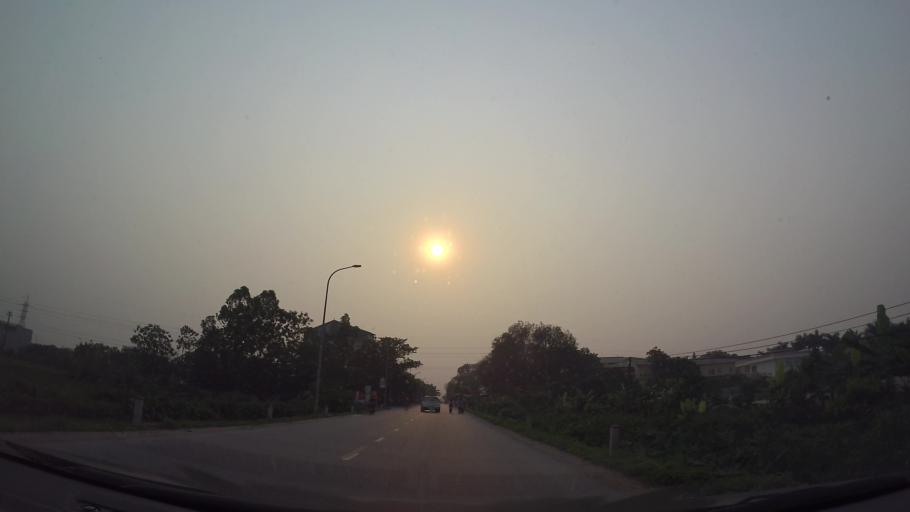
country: VN
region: Ha Noi
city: Thuong Tin
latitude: 20.8684
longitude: 105.8453
